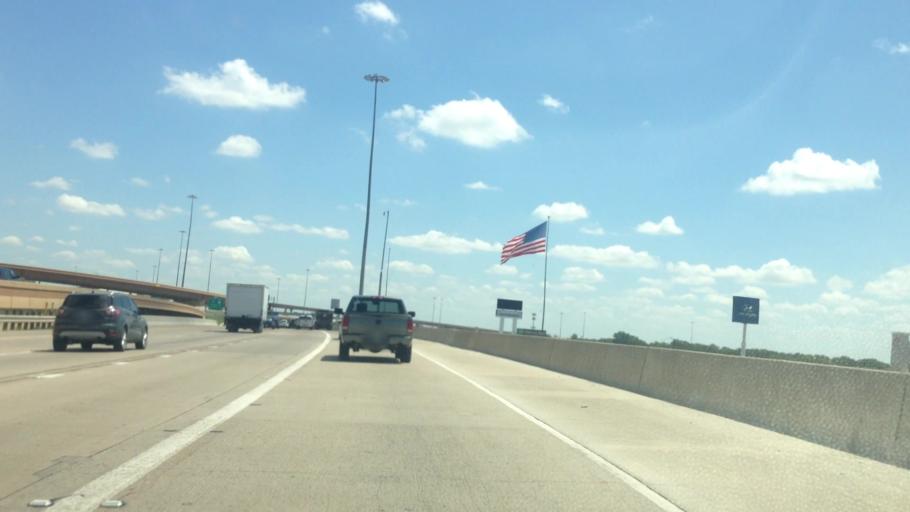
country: US
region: Texas
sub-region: Tarrant County
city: North Richland Hills
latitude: 32.8328
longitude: -97.2177
